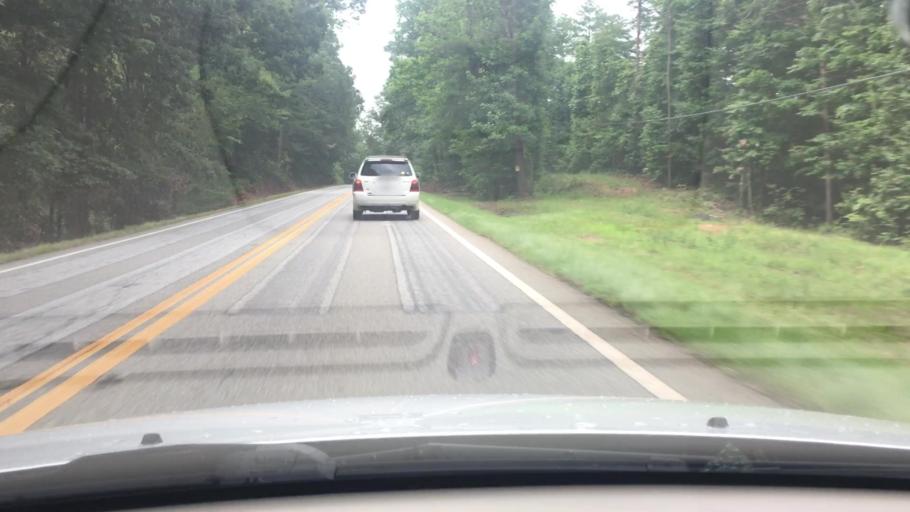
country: US
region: Georgia
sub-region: Dawson County
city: Dawsonville
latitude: 34.4214
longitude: -84.0379
